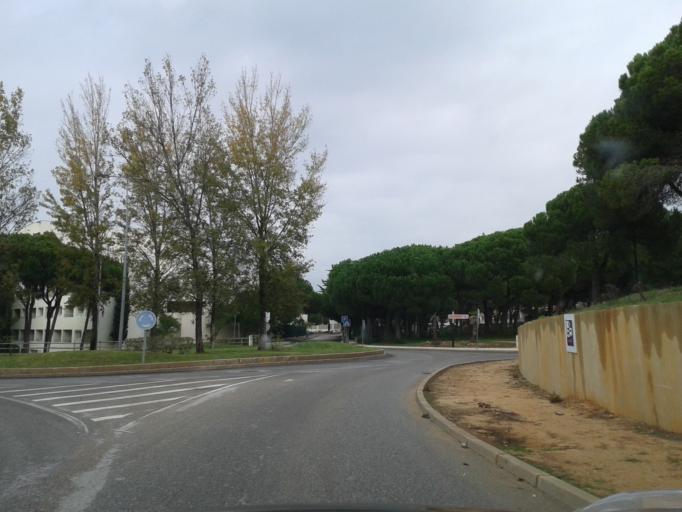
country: PT
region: Faro
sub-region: Loule
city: Boliqueime
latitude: 37.0942
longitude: -8.1715
